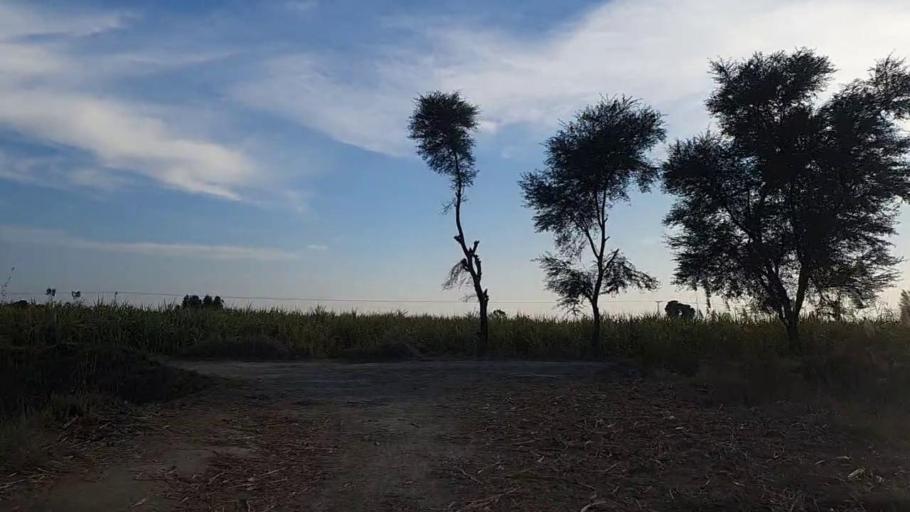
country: PK
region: Sindh
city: Bandhi
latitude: 26.5506
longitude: 68.2808
